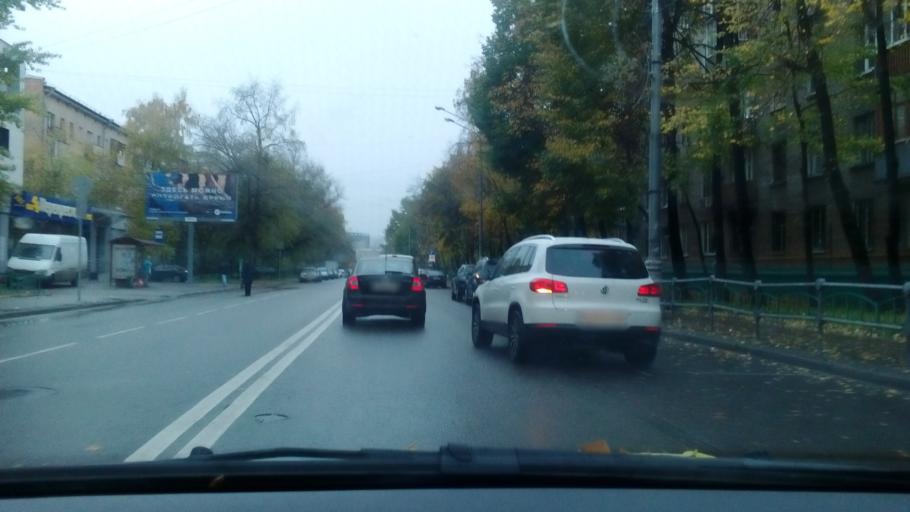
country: RU
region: Moscow
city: Mar'ina Roshcha
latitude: 55.7976
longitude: 37.5761
